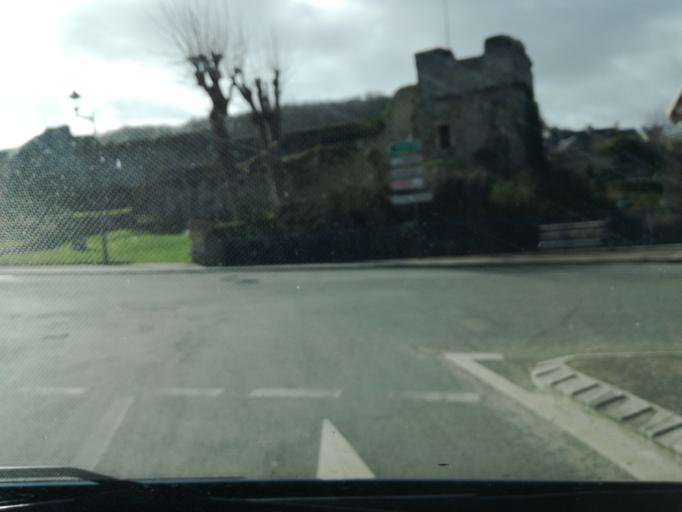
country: FR
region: Haute-Normandie
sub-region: Departement de la Seine-Maritime
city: Fecamp
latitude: 49.7555
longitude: 0.3799
